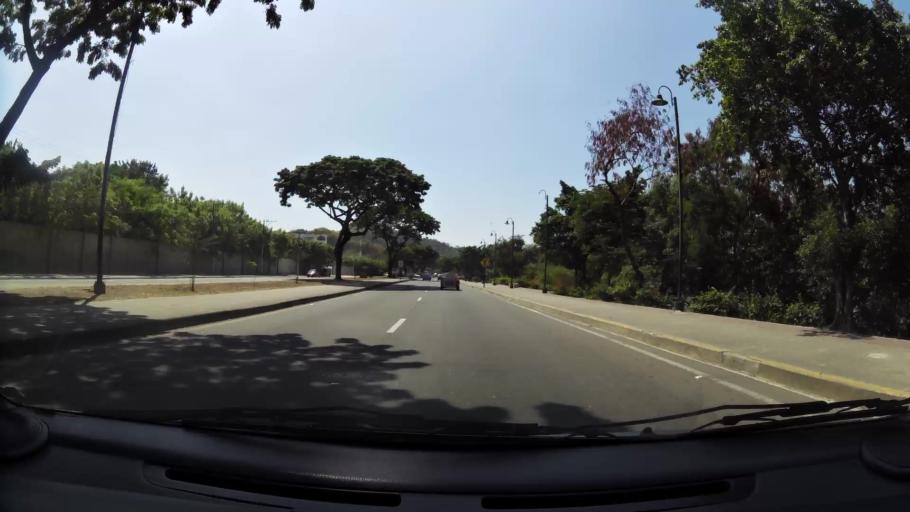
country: EC
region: Guayas
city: Guayaquil
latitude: -2.1927
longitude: -79.9346
